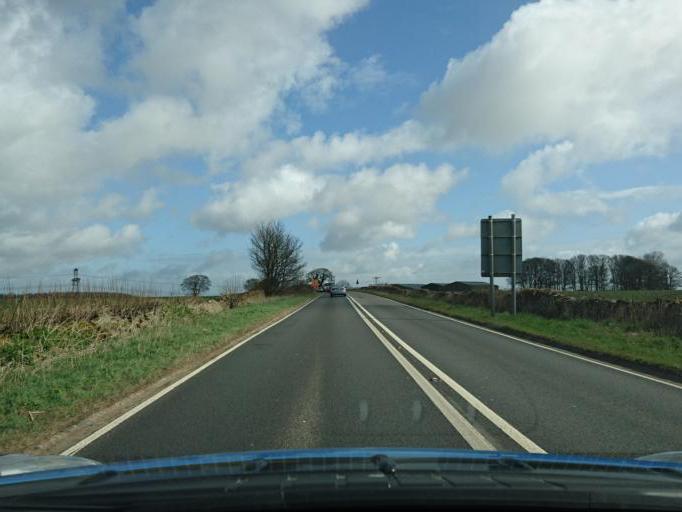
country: GB
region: England
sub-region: South Gloucestershire
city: Hinton
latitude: 51.4885
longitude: -2.3588
